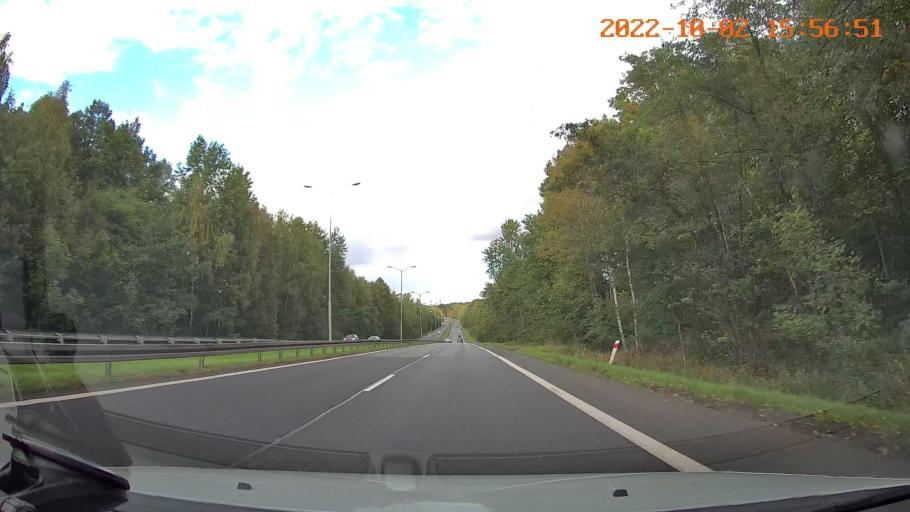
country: PL
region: Silesian Voivodeship
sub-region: Katowice
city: Murcki
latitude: 50.2091
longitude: 19.0530
